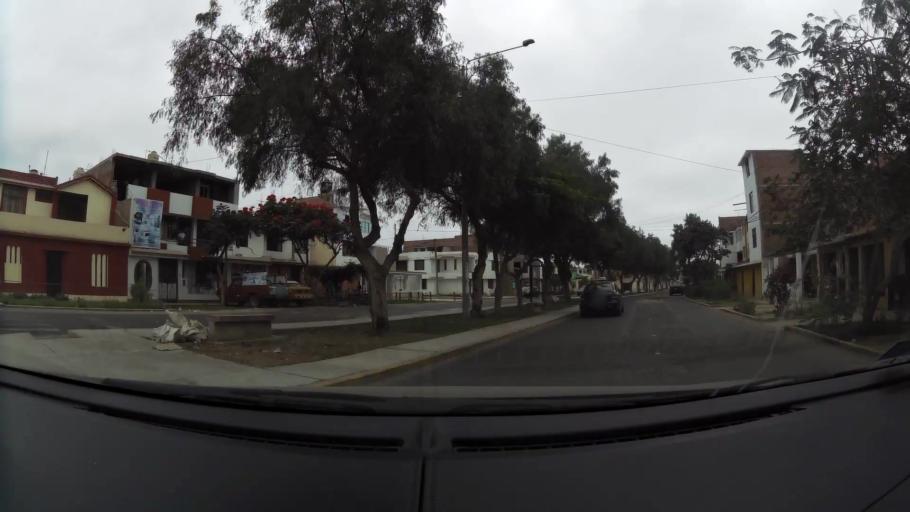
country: PE
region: La Libertad
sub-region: Provincia de Trujillo
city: Trujillo
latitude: -8.1113
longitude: -79.0400
